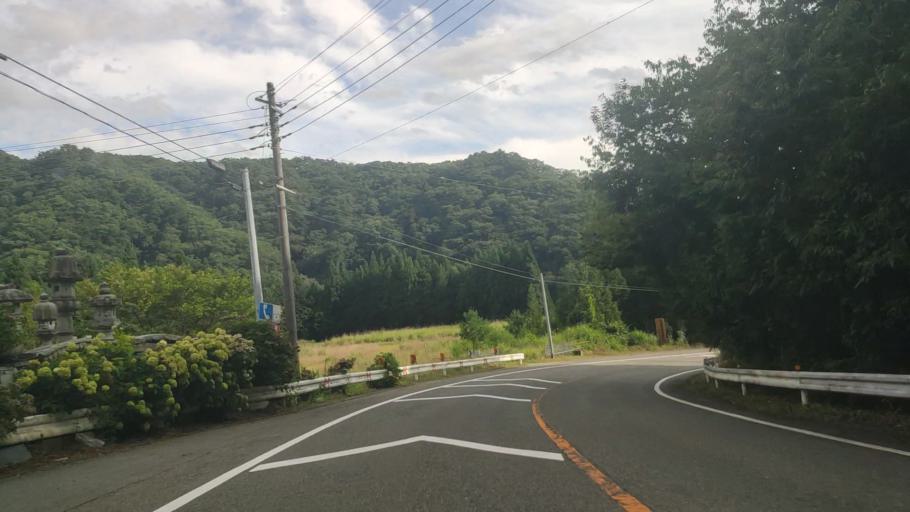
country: JP
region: Gunma
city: Kiryu
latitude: 36.5950
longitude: 139.4039
